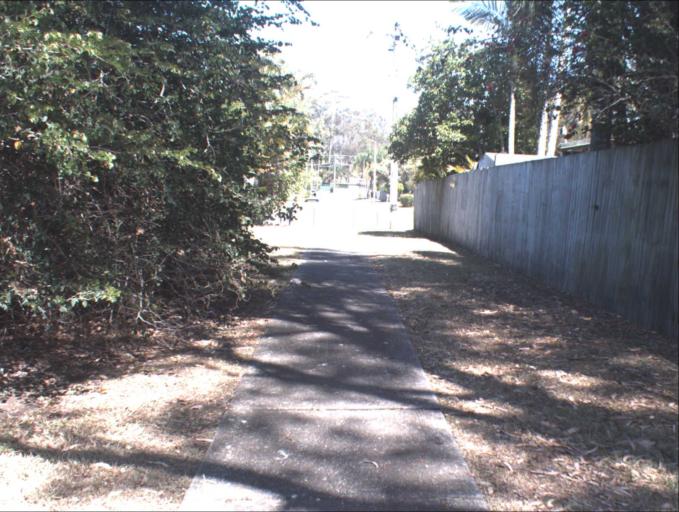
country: AU
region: Queensland
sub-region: Gold Coast
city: Yatala
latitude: -27.7028
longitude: 153.2245
